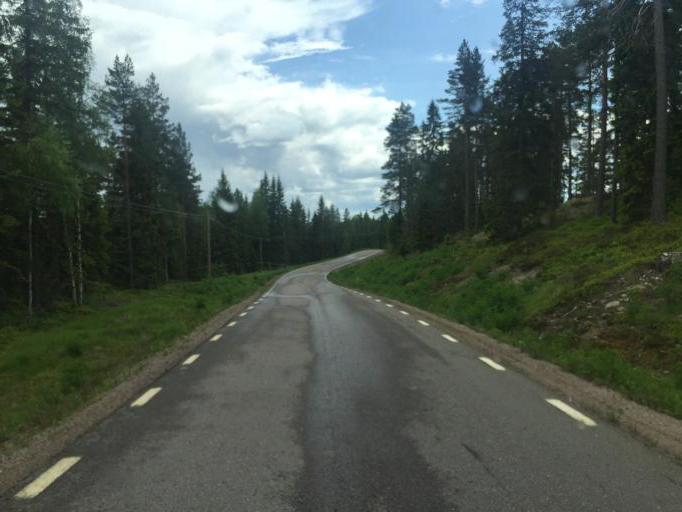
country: SE
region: Vaermland
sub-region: Hagfors Kommun
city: Hagfors
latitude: 60.2996
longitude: 13.8671
